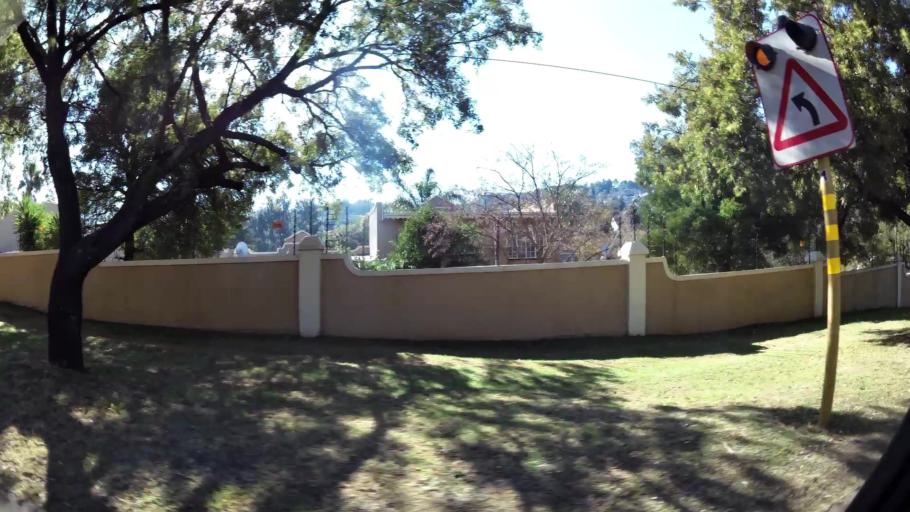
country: ZA
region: Gauteng
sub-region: City of Johannesburg Metropolitan Municipality
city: Roodepoort
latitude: -26.1218
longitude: 27.8735
